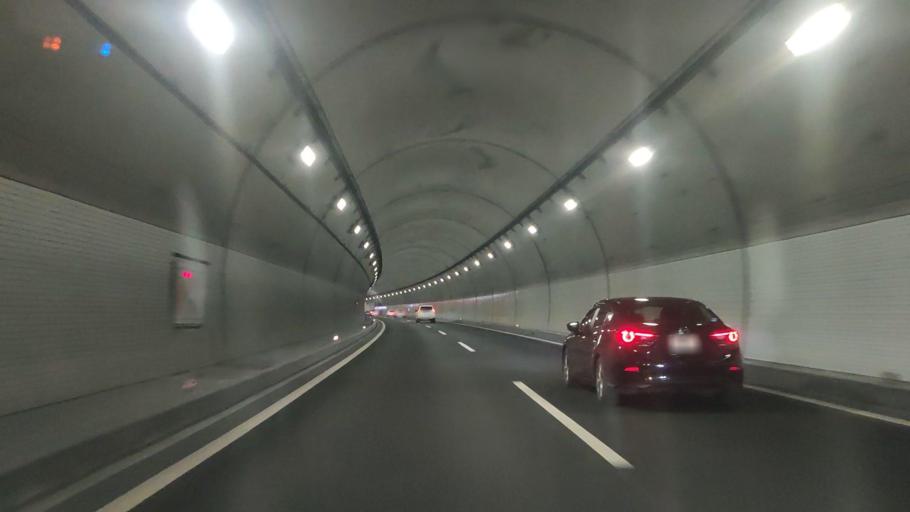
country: JP
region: Fukuoka
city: Kanda
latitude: 33.8037
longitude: 130.9434
